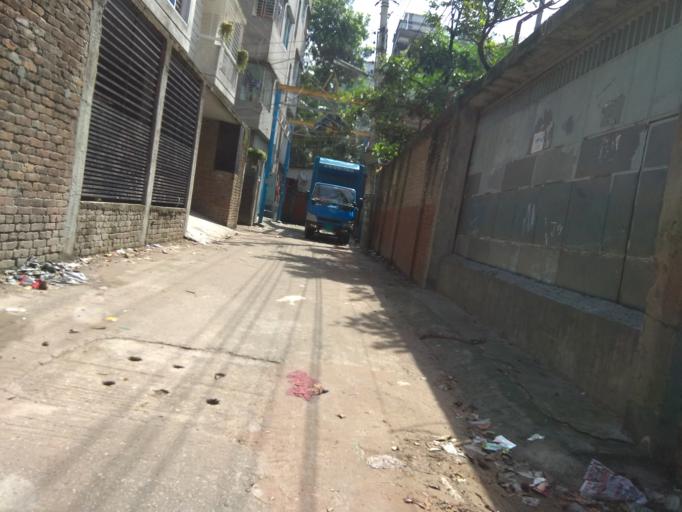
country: BD
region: Dhaka
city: Azimpur
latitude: 23.7987
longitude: 90.3570
